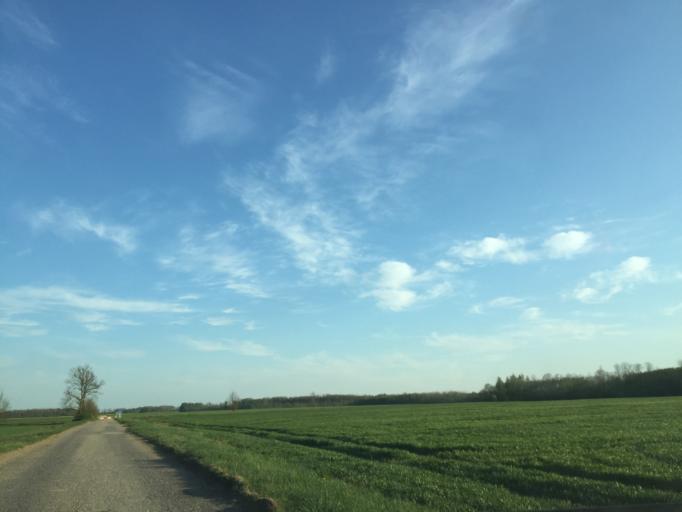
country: LV
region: Bauskas Rajons
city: Bauska
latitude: 56.2831
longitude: 24.2650
